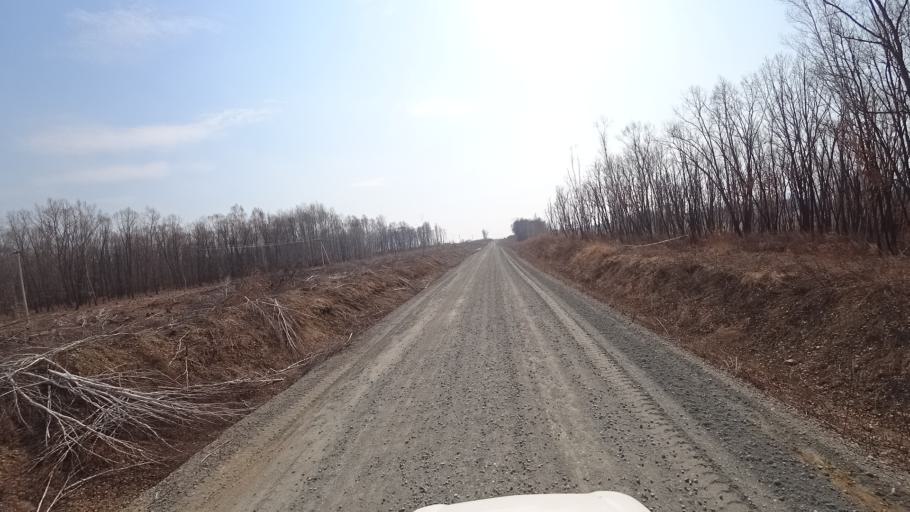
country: RU
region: Amur
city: Novobureyskiy
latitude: 49.8216
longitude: 129.9831
